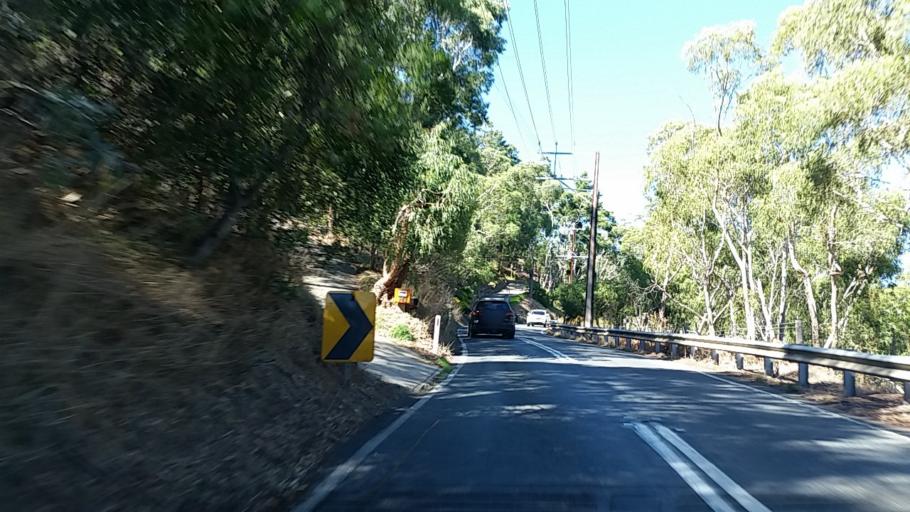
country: AU
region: South Australia
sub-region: Burnside
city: Beaumont
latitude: -34.9508
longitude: 138.6890
